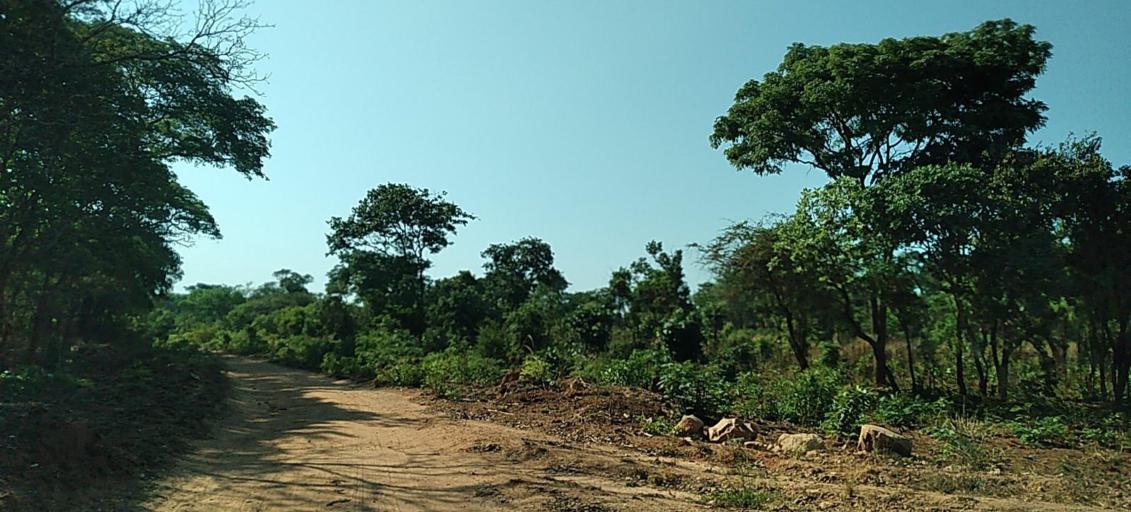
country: ZM
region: Central
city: Mkushi
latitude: -13.4663
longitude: 28.9148
